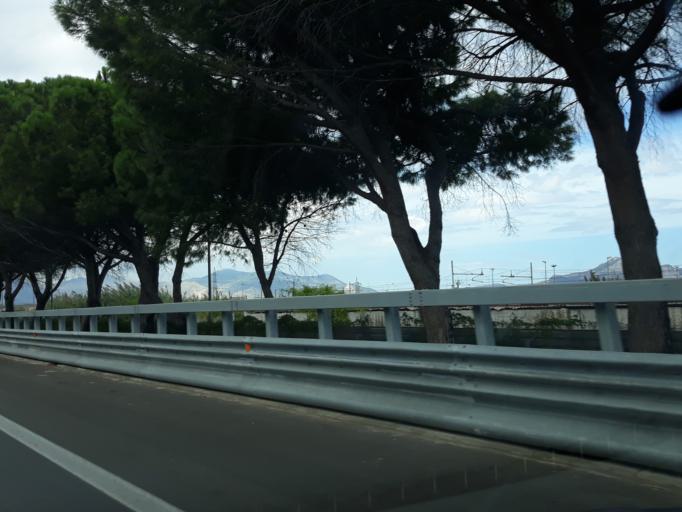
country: IT
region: Sicily
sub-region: Palermo
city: Ciaculli
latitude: 38.0861
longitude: 13.4109
